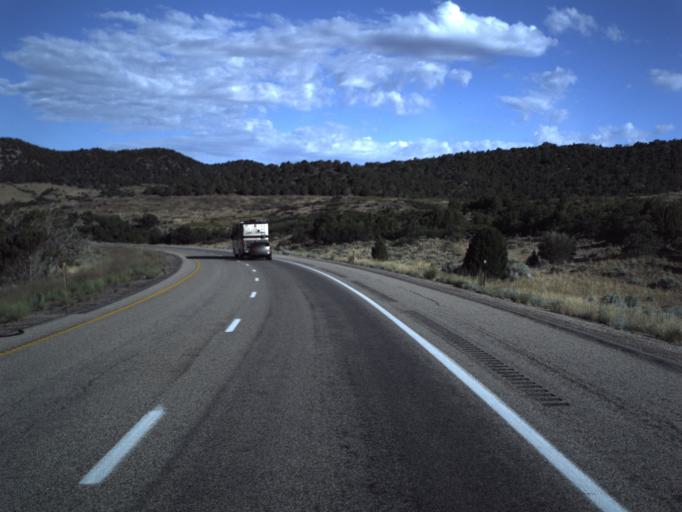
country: US
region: Utah
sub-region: Beaver County
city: Beaver
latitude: 38.6065
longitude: -112.5076
